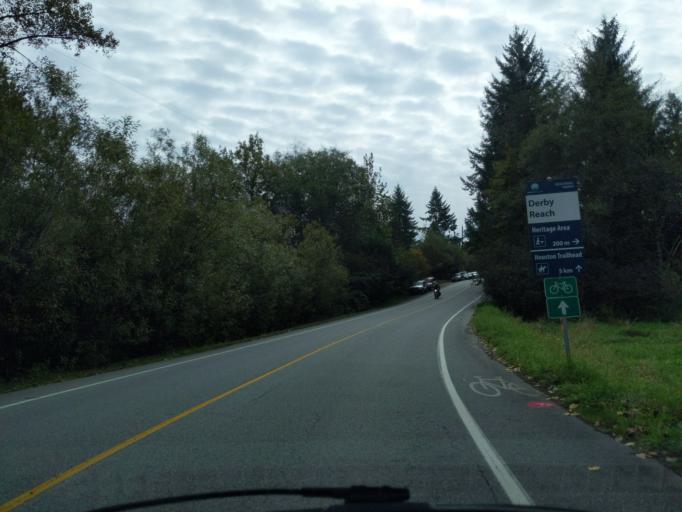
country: CA
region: British Columbia
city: Maple Ridge
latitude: 49.1995
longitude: -122.5944
